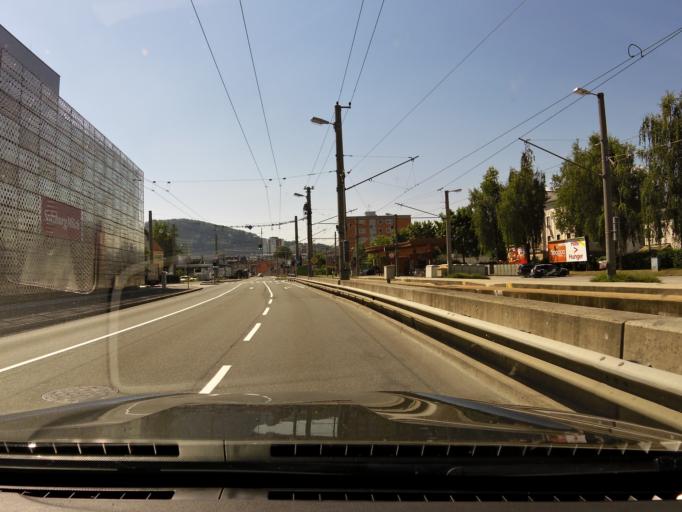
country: AT
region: Salzburg
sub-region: Politischer Bezirk Salzburg-Umgebung
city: Bergheim
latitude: 47.8199
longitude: 13.0408
